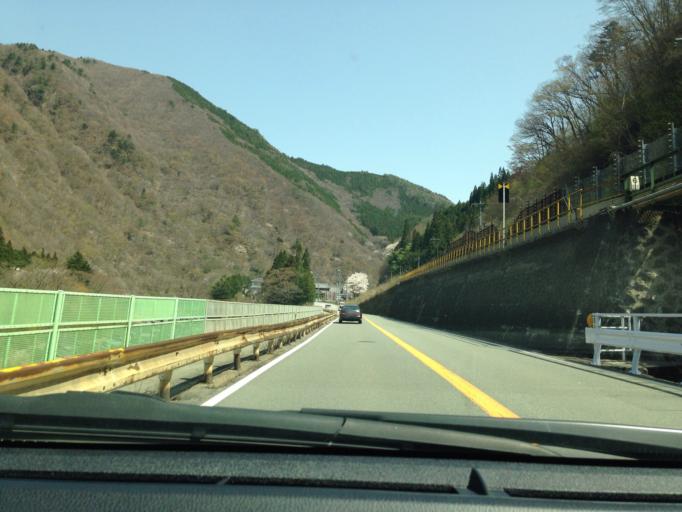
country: JP
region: Gifu
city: Takayama
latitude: 35.9731
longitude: 137.2659
